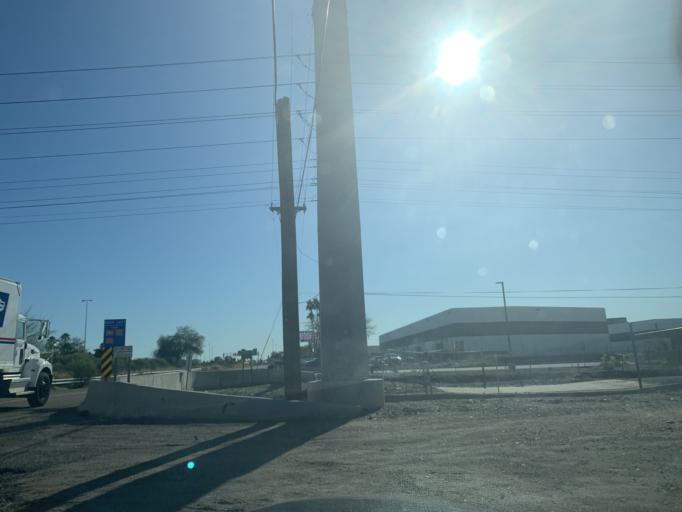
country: US
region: Arizona
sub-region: Maricopa County
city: Tempe Junction
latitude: 33.4170
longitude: -111.9788
